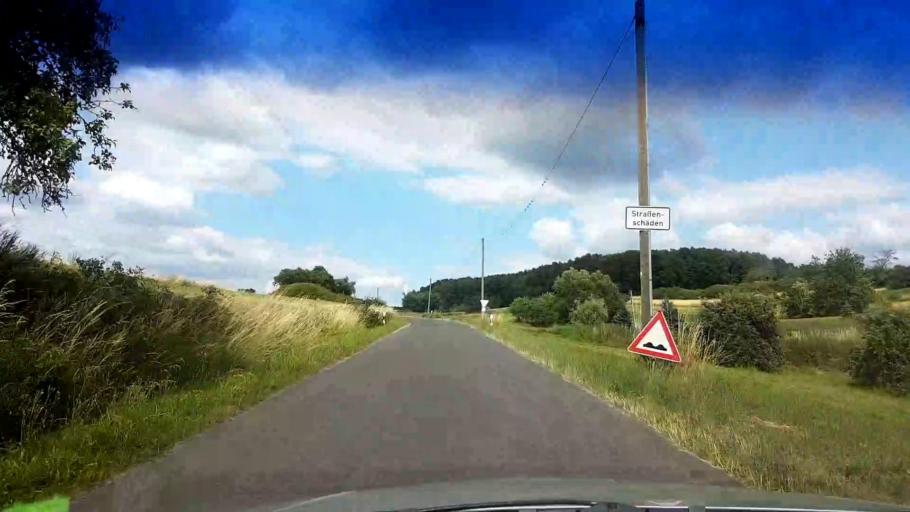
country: DE
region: Bavaria
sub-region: Upper Franconia
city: Lauter
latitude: 49.9916
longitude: 10.7599
